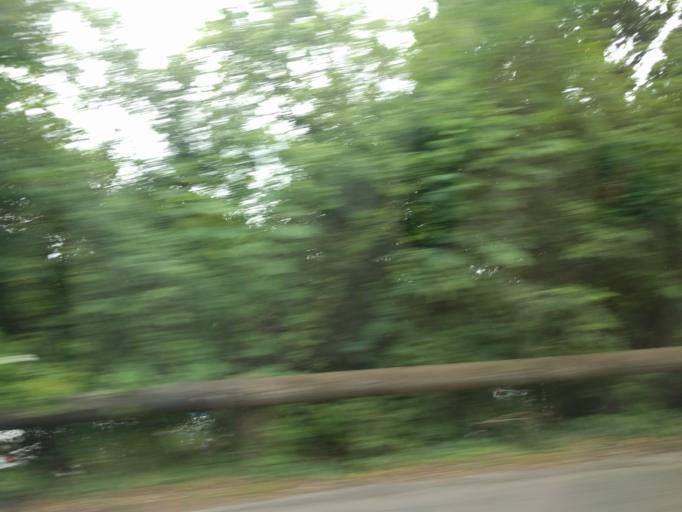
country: GB
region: England
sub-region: Hampshire
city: Totton
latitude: 50.8918
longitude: -1.5243
